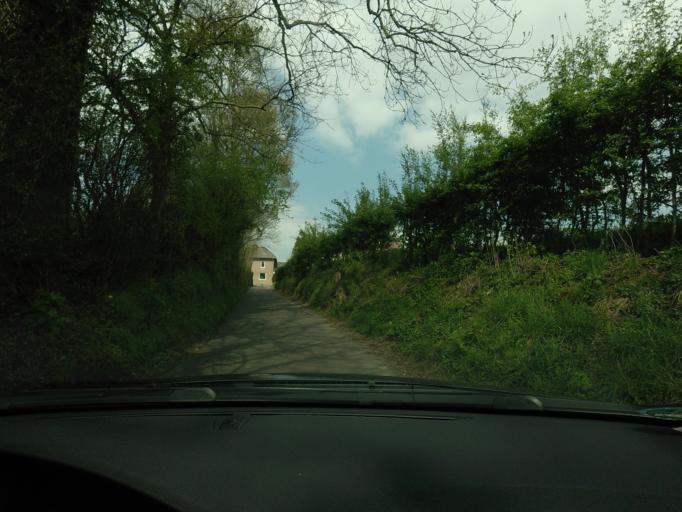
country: NL
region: Limburg
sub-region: Eijsden-Margraten
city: Margraten
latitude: 50.7883
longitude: 5.8090
